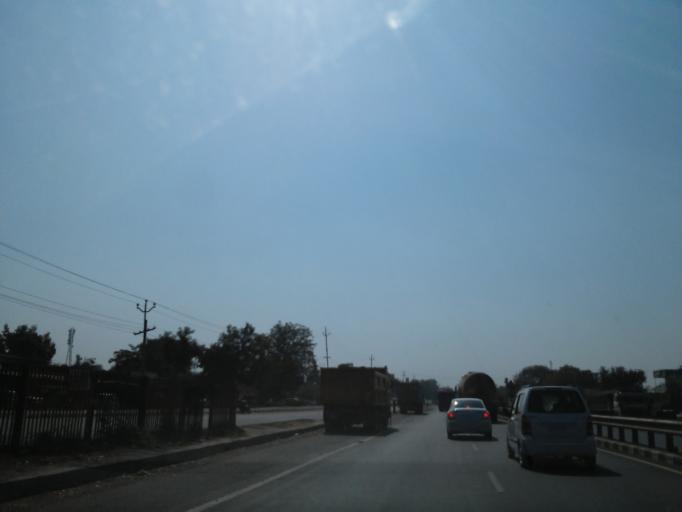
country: IN
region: Gujarat
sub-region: Gandhinagar
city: Ghandinagar
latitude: 23.2302
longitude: 72.7325
